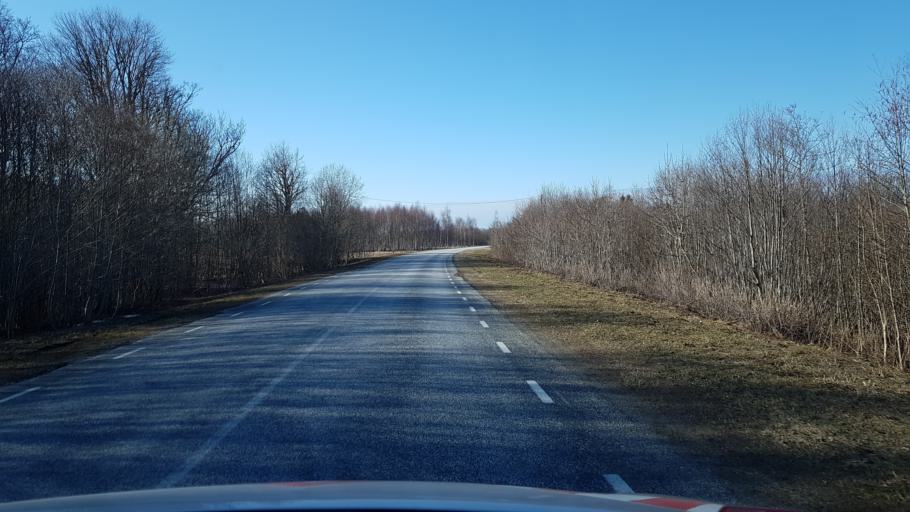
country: EE
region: Laeaene-Virumaa
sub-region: Haljala vald
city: Haljala
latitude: 59.4770
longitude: 26.1595
